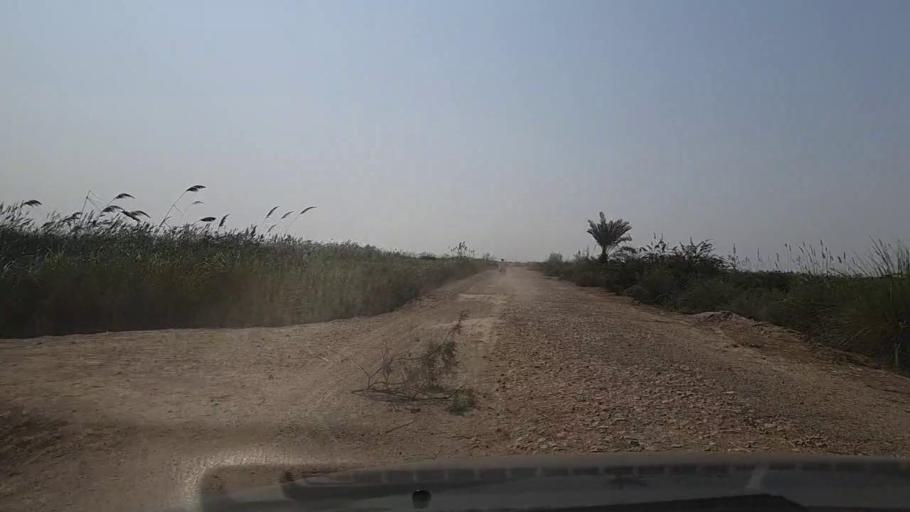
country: PK
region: Sindh
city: Mirpur Sakro
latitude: 24.3741
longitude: 67.6540
